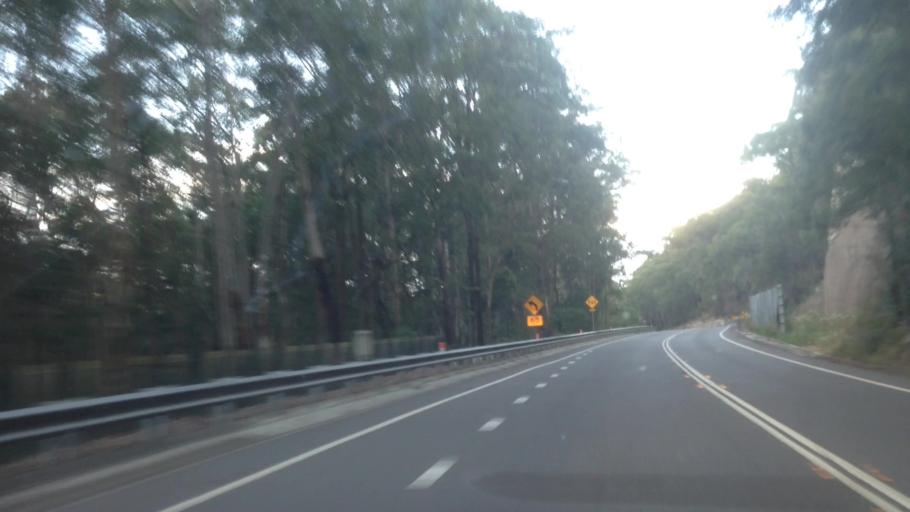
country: AU
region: New South Wales
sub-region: Lake Macquarie Shire
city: Cooranbong
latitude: -32.9659
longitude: 151.4796
